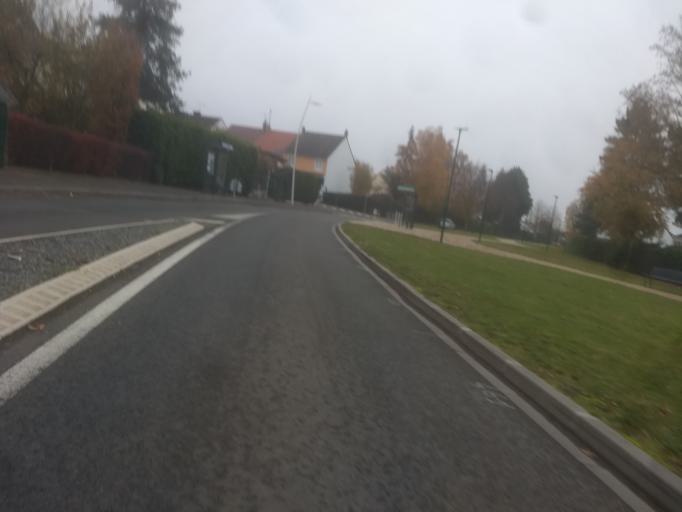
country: FR
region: Nord-Pas-de-Calais
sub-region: Departement du Pas-de-Calais
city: Saint-Laurent-Blangy
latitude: 50.3050
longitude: 2.7976
